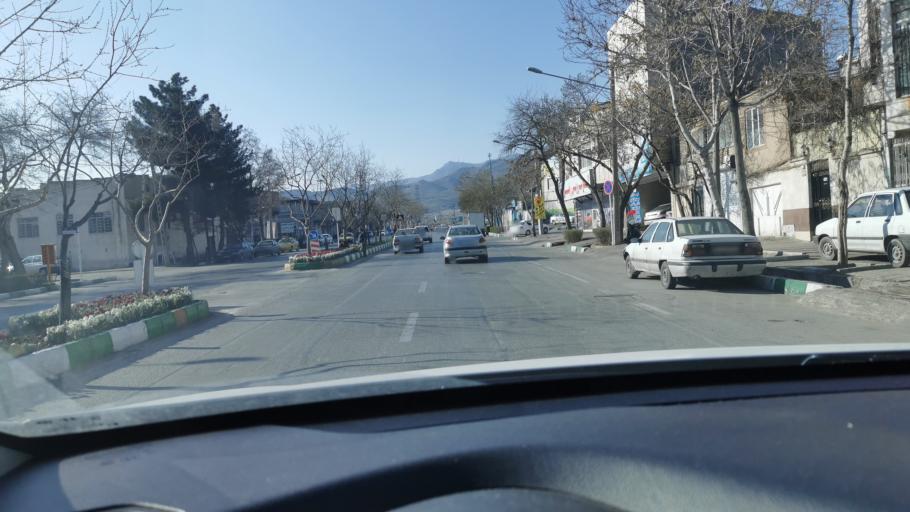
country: IR
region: Razavi Khorasan
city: Mashhad
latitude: 36.2721
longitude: 59.5757
